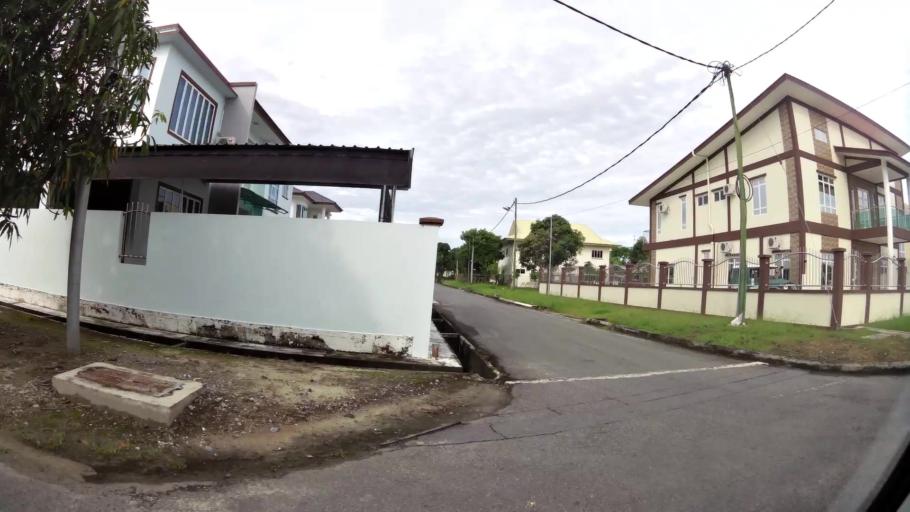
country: BN
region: Belait
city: Seria
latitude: 4.6134
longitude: 114.3622
